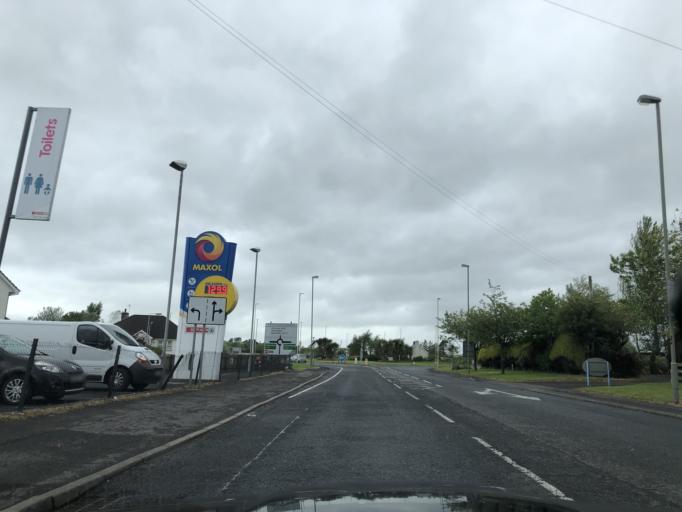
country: GB
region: Northern Ireland
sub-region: Ballymoney District
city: Ballymoney
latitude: 55.0803
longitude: -6.5247
